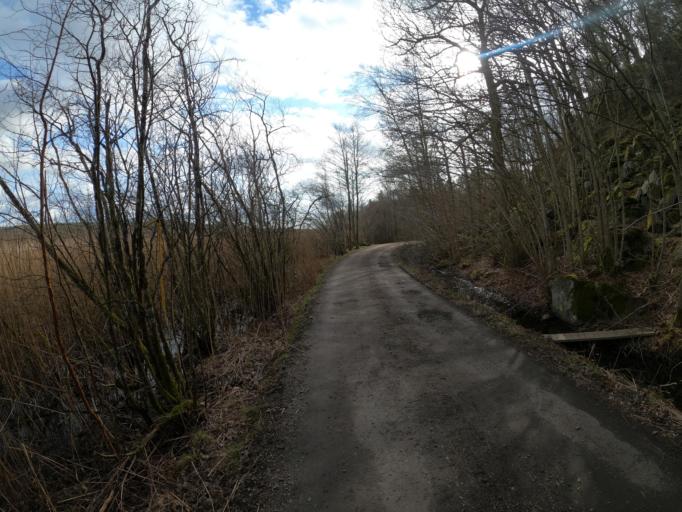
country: SE
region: Vaestra Goetaland
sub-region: Harryda Kommun
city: Molnlycke
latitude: 57.6320
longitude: 12.0972
